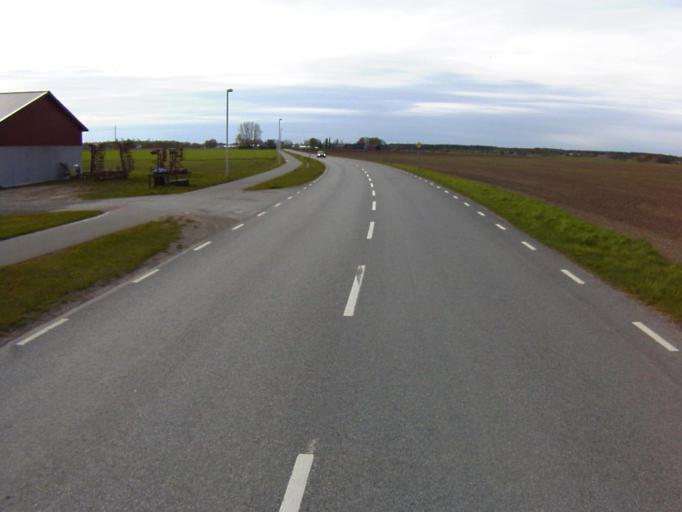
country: SE
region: Skane
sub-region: Kristianstads Kommun
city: Kristianstad
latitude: 56.0100
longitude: 14.1261
